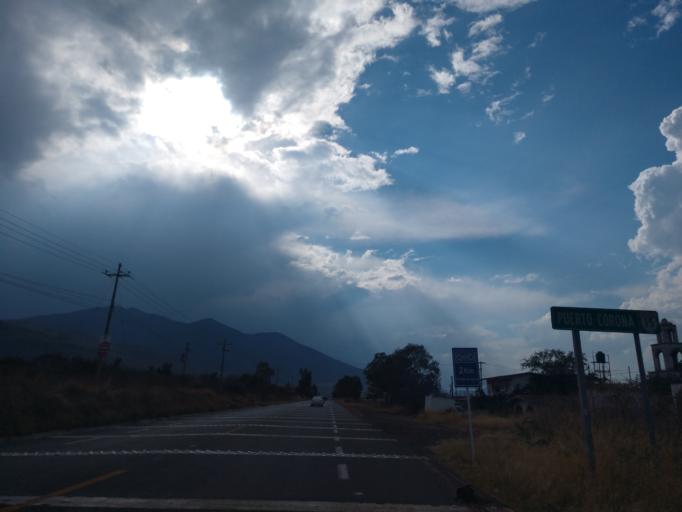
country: MX
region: Jalisco
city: Ajijic
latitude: 20.1942
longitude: -103.2786
